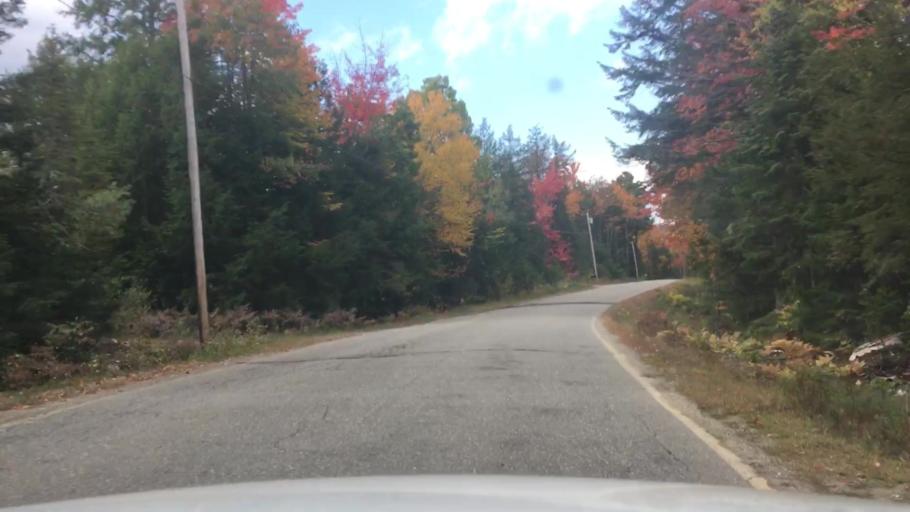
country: US
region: Maine
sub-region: Knox County
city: Washington
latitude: 44.3288
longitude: -69.3678
